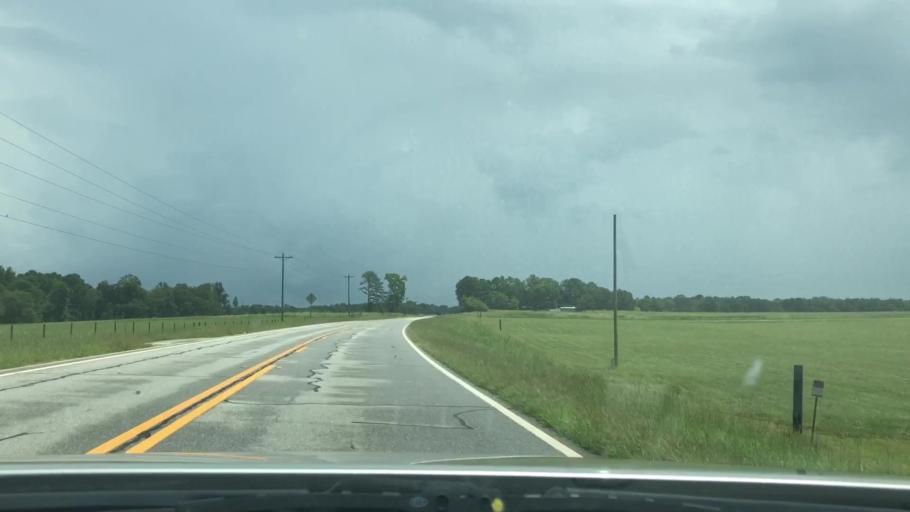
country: US
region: Georgia
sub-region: Pike County
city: Zebulon
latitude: 33.1056
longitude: -84.3091
